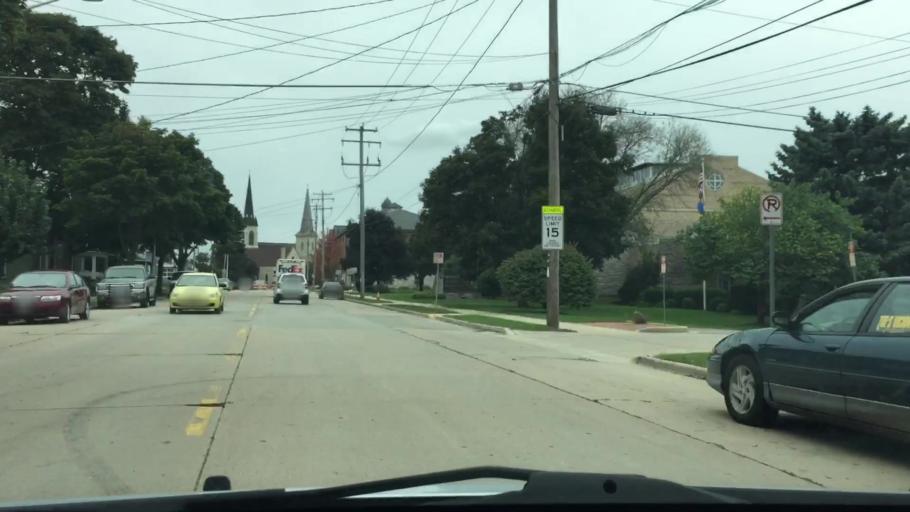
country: US
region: Wisconsin
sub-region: Waukesha County
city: Waukesha
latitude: 43.0151
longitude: -88.2243
